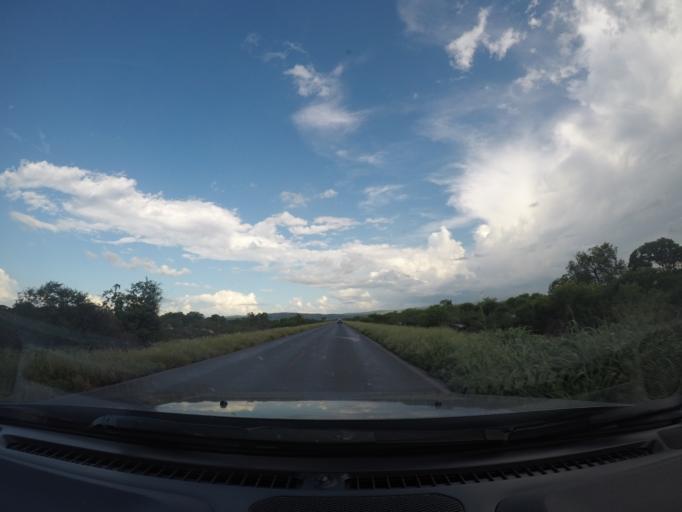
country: BR
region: Bahia
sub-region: Ibotirama
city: Ibotirama
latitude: -12.1784
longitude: -43.2441
